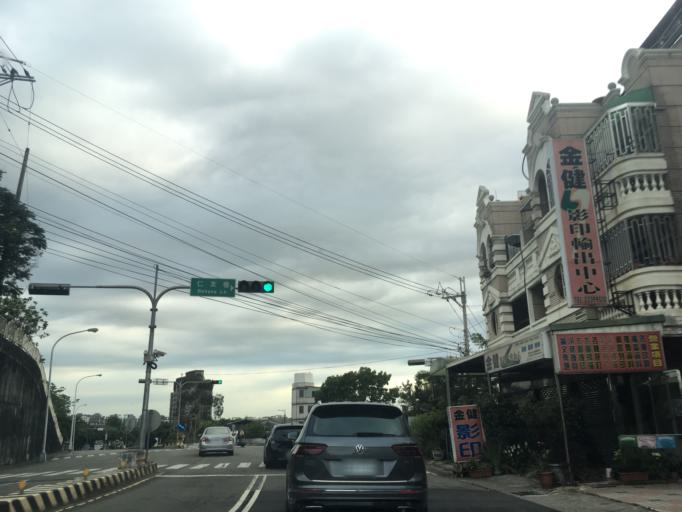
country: TW
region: Taiwan
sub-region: Taichung City
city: Taichung
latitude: 24.1740
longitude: 120.7346
